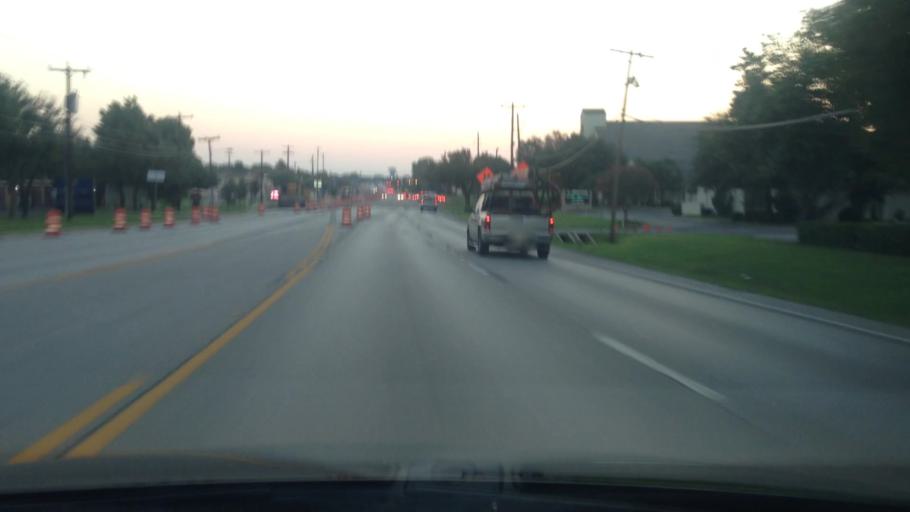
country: US
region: Texas
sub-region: Tarrant County
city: Colleyville
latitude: 32.8723
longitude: -97.1658
